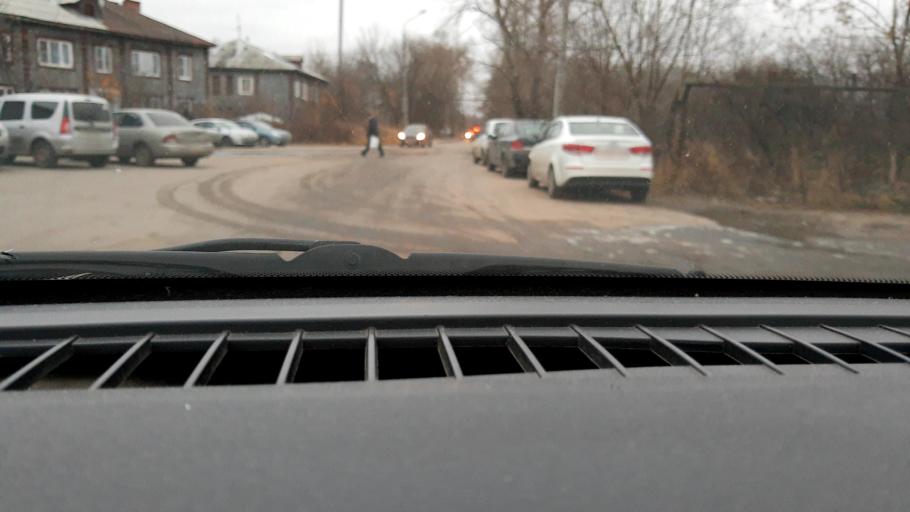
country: RU
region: Nizjnij Novgorod
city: Nizhniy Novgorod
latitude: 56.3052
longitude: 43.8796
